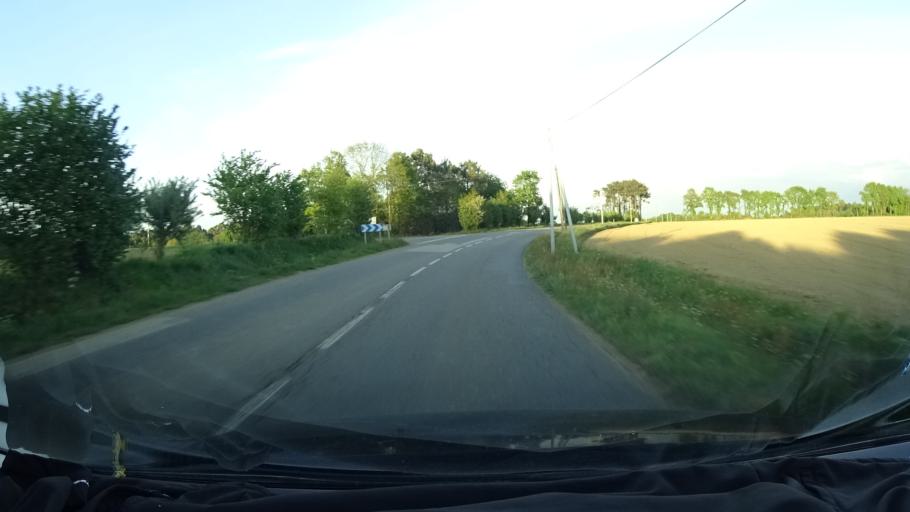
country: FR
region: Brittany
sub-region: Departement du Morbihan
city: Peaule
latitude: 47.5945
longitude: -2.3242
